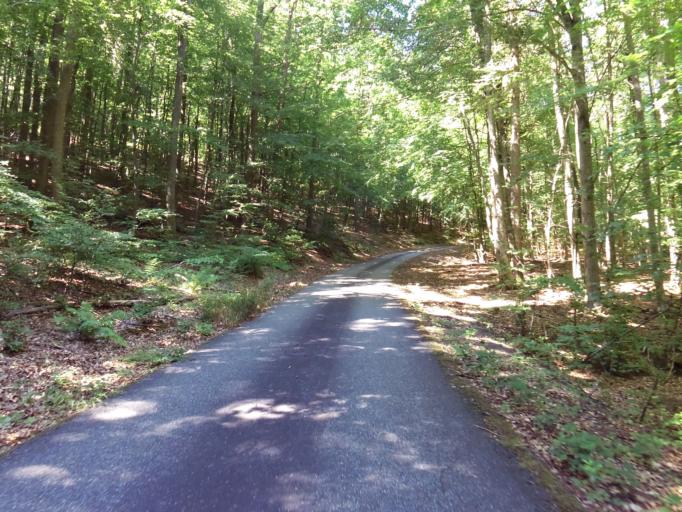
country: DE
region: Rheinland-Pfalz
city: Elmstein
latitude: 49.3826
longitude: 7.9484
